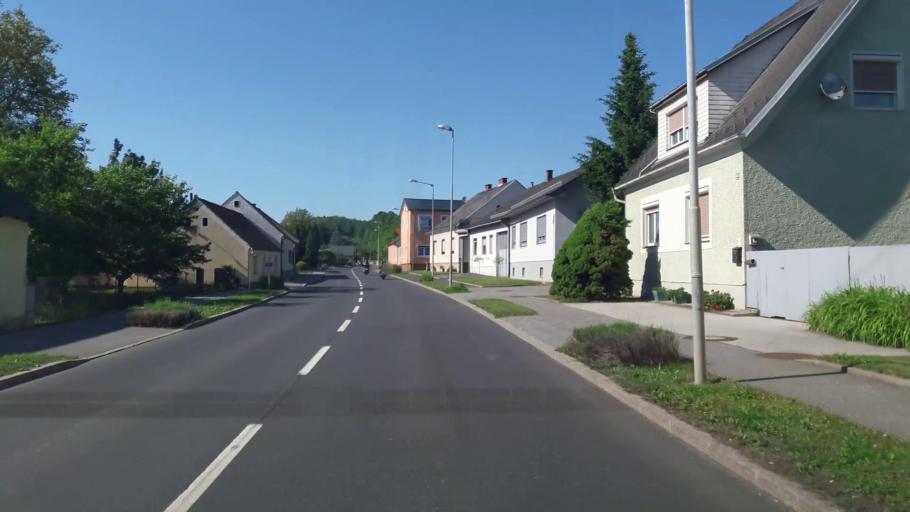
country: AT
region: Burgenland
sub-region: Politischer Bezirk Gussing
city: Ollersdorf im Burgenland
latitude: 47.1853
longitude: 16.1643
